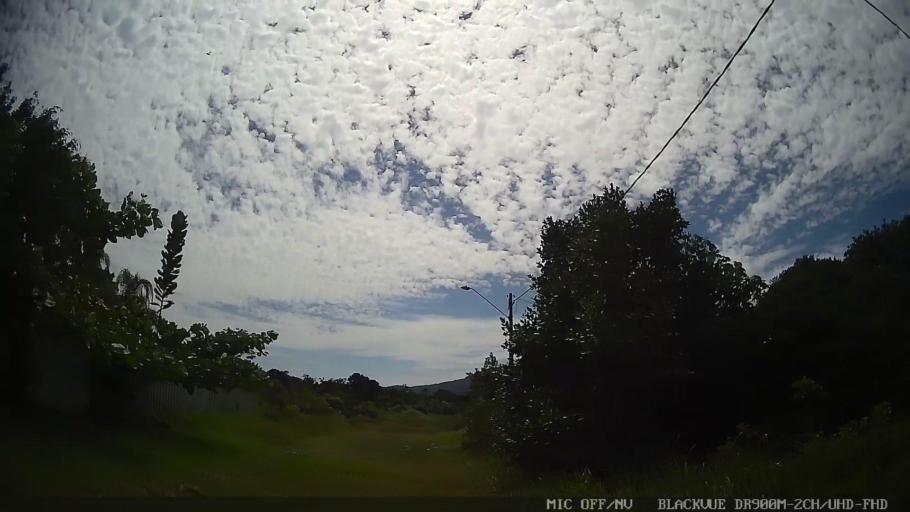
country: BR
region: Sao Paulo
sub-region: Iguape
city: Iguape
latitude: -24.7170
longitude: -47.5078
